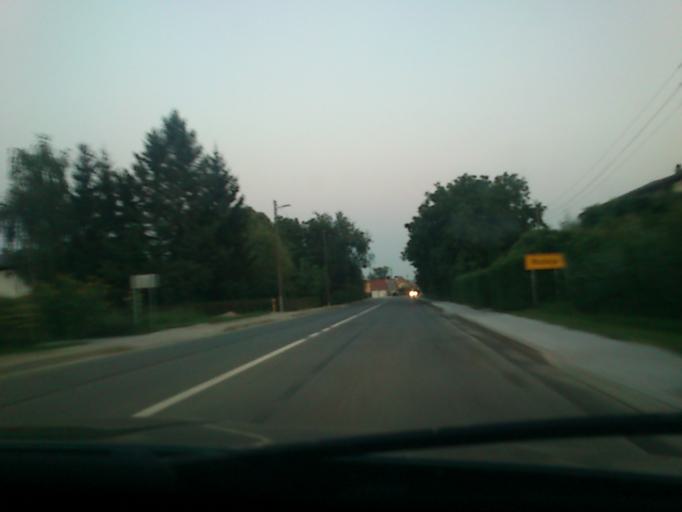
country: SI
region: Duplek
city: Spodnji Duplek
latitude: 46.4805
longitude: 15.7426
